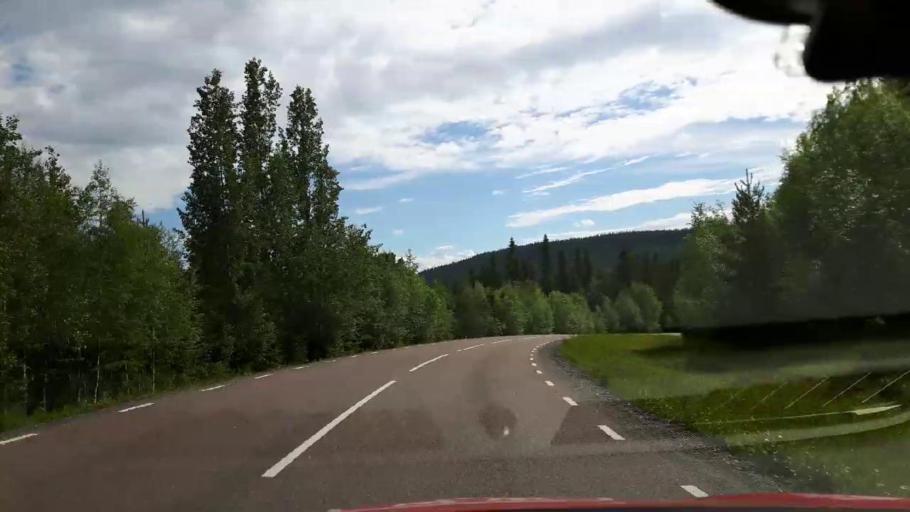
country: SE
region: Jaemtland
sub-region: Krokoms Kommun
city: Valla
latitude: 63.9360
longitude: 14.2213
